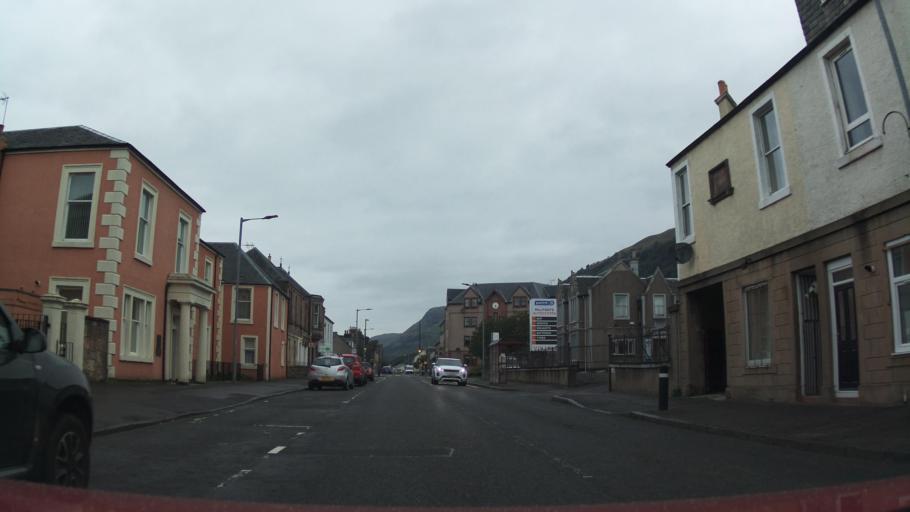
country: GB
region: Scotland
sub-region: Clackmannanshire
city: Tillicoultry
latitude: 56.1534
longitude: -3.7432
